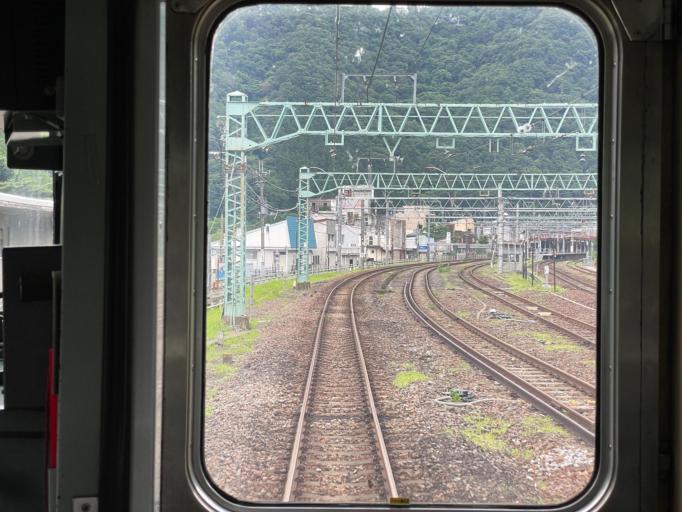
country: JP
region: Gunma
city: Numata
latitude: 36.7759
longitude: 138.9696
